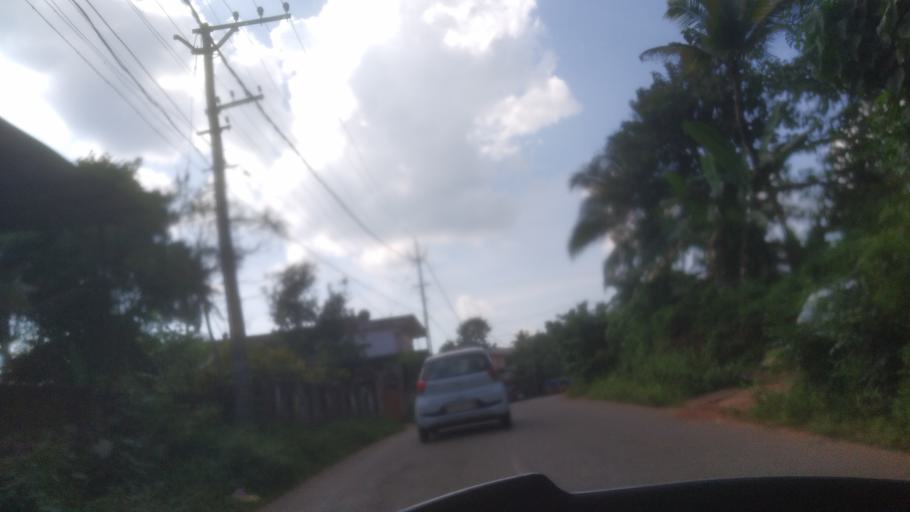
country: IN
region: Kerala
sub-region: Ernakulam
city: Muvattupula
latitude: 9.9952
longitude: 76.6041
